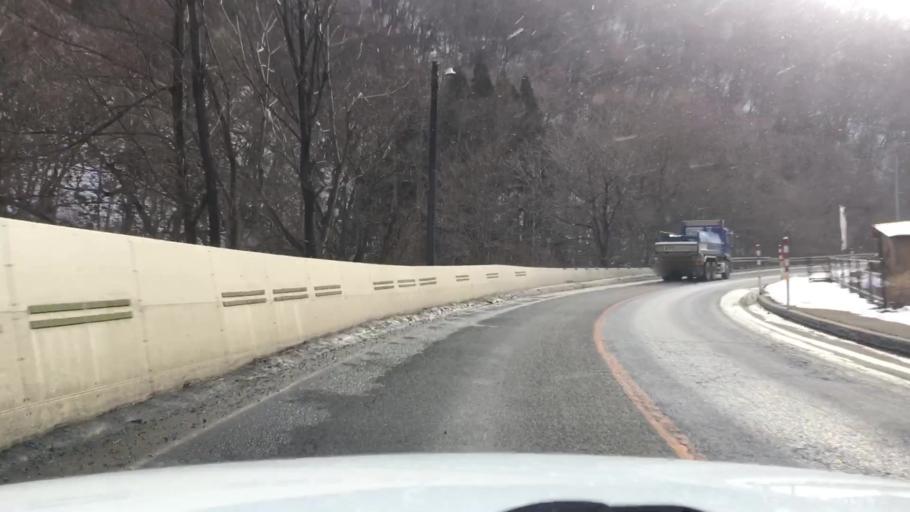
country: JP
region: Iwate
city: Tono
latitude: 39.6243
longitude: 141.5140
